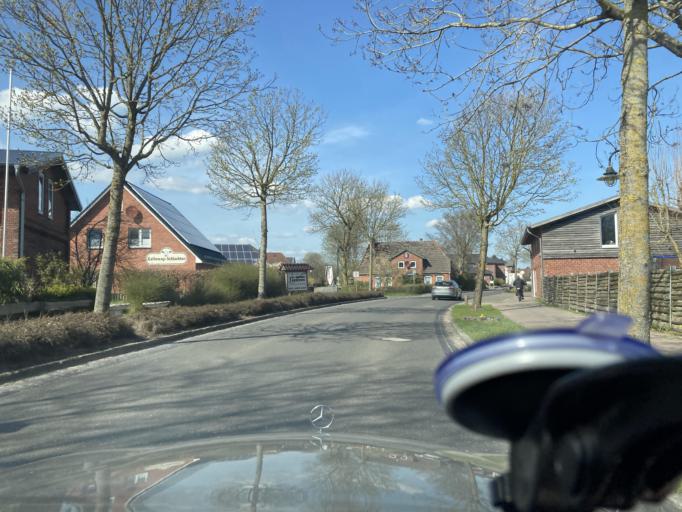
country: DE
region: Schleswig-Holstein
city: Lehe
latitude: 54.3363
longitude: 9.0224
